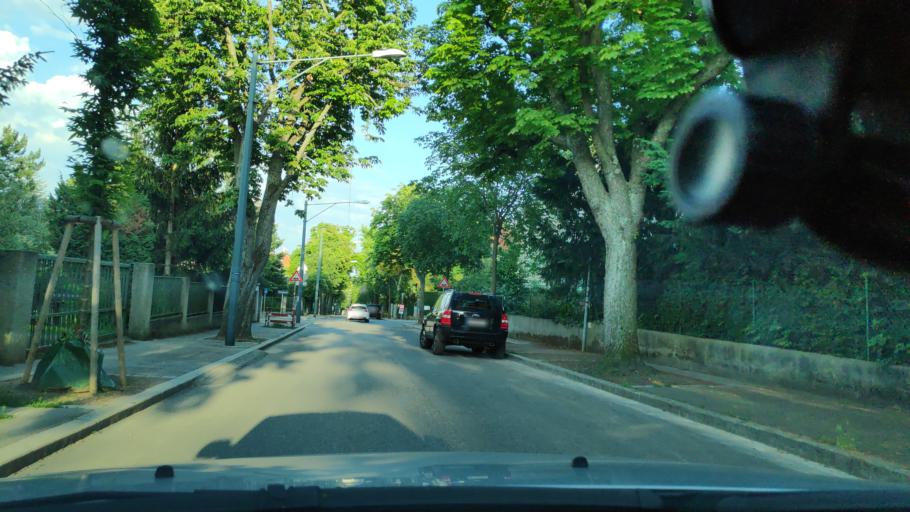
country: AT
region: Vienna
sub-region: Wien Stadt
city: Vienna
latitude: 48.2264
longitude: 16.3016
